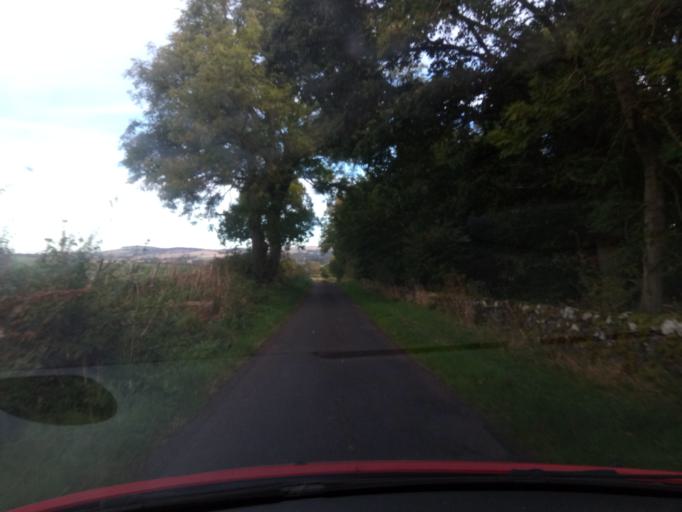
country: GB
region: Scotland
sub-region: The Scottish Borders
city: Kelso
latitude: 55.5154
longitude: -2.3902
